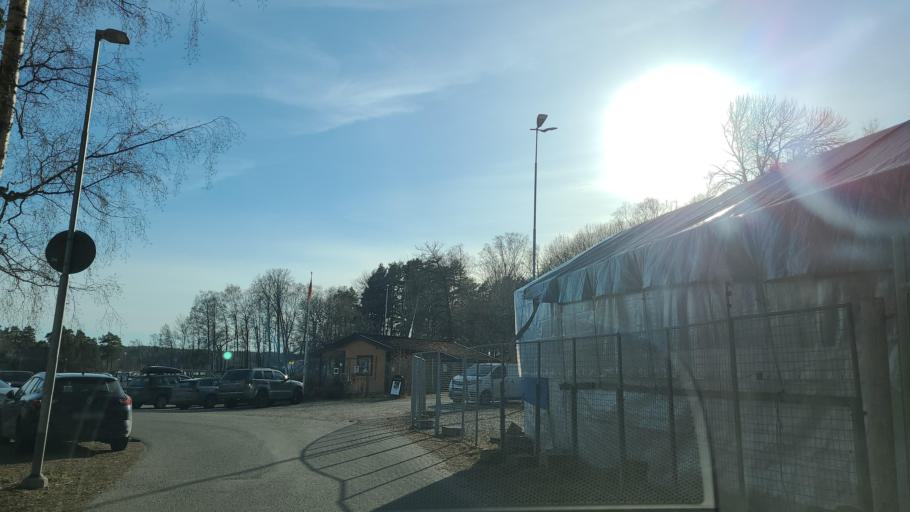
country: SE
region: Stockholm
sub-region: Ekero Kommun
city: Ekeroe
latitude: 59.2670
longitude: 17.7795
